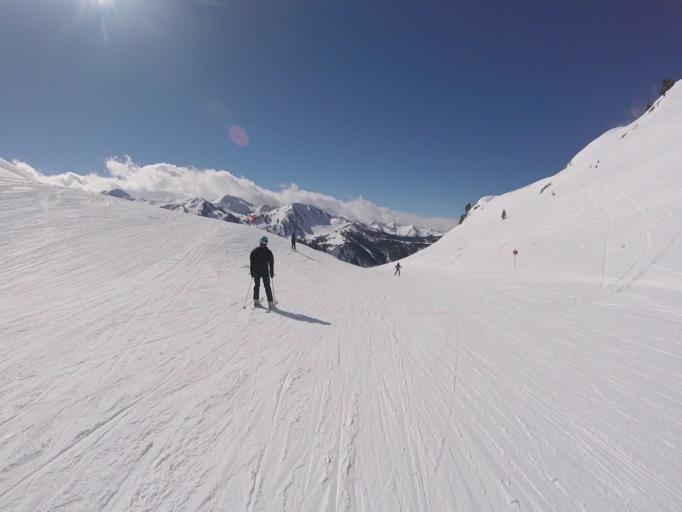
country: ES
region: Catalonia
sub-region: Provincia de Lleida
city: Espot
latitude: 42.6693
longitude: 0.9832
